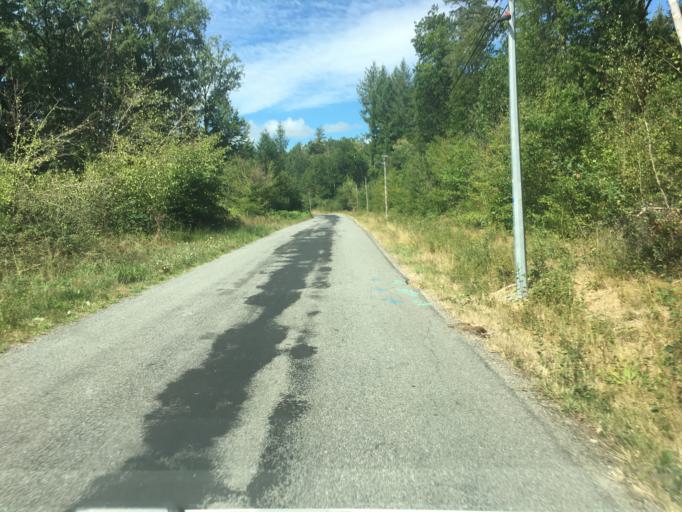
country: FR
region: Auvergne
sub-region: Departement du Cantal
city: Champagnac
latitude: 45.4264
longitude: 2.3679
